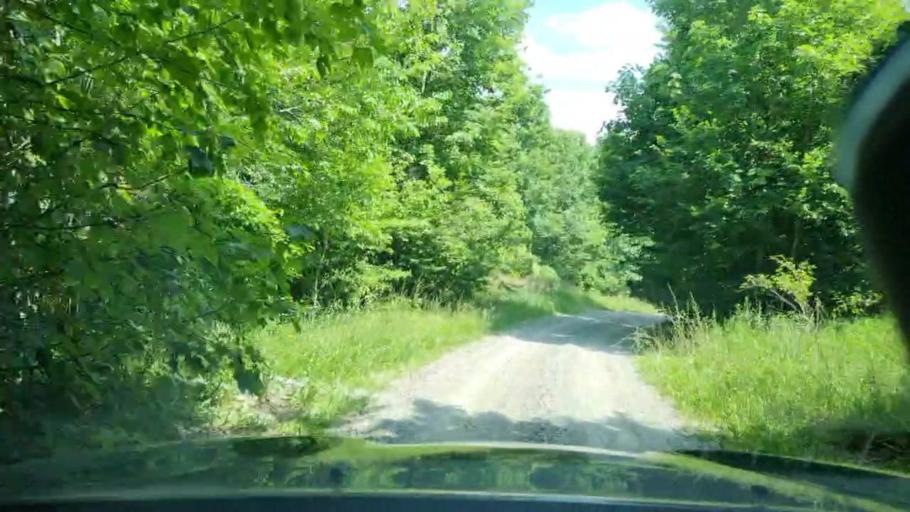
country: BA
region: Federation of Bosnia and Herzegovina
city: Bosansko Grahovo
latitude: 44.3265
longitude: 16.2327
